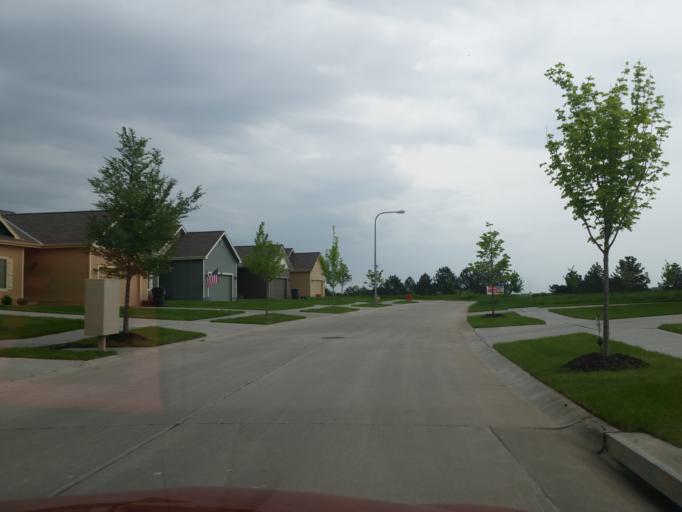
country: US
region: Nebraska
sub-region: Douglas County
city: Bennington
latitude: 41.3218
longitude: -96.1342
